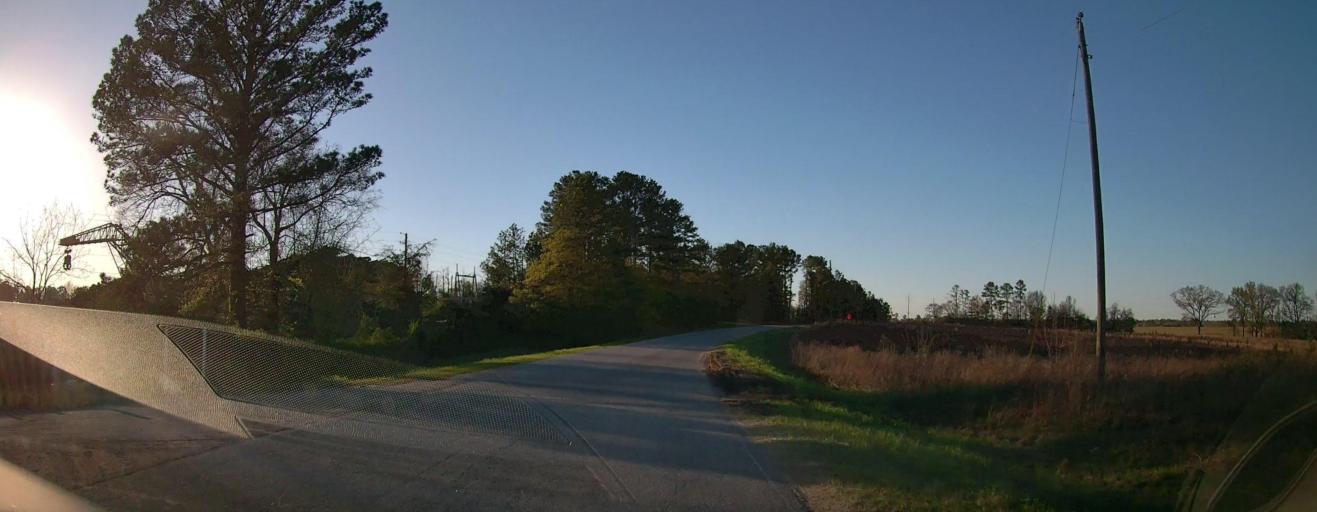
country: US
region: Georgia
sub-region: Wilkinson County
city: Gordon
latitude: 32.8908
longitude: -83.2999
